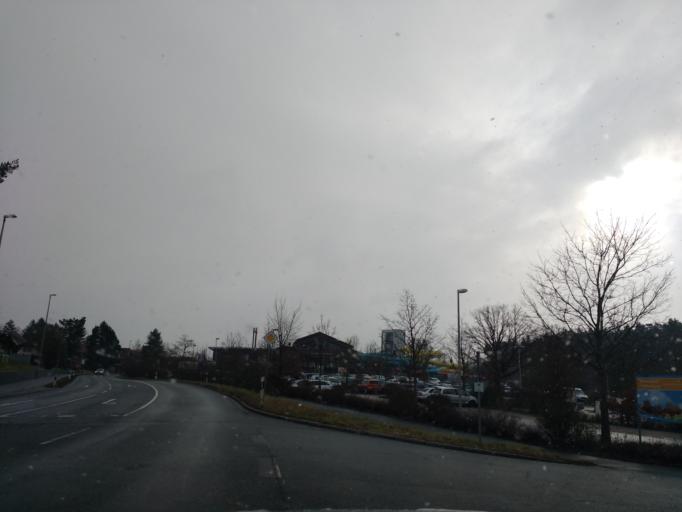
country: DE
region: Bavaria
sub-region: Regierungsbezirk Mittelfranken
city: Herzogenaurach
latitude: 49.5736
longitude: 10.8654
